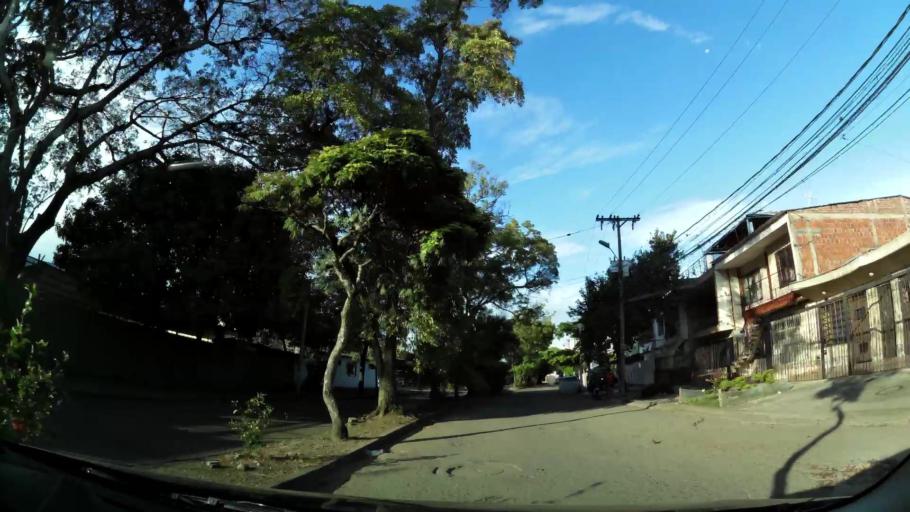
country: CO
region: Valle del Cauca
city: Cali
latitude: 3.4321
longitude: -76.5141
